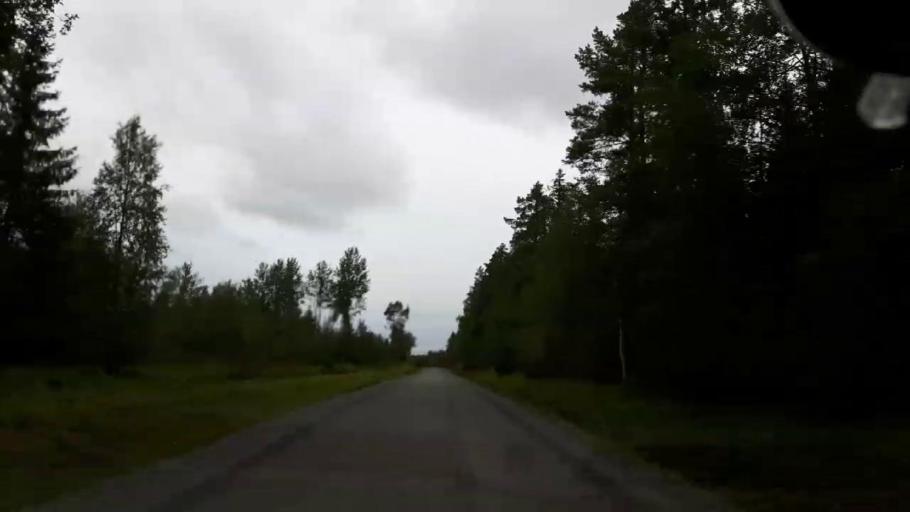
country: SE
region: Jaemtland
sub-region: OEstersunds Kommun
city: Ostersund
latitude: 63.1020
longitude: 14.5461
